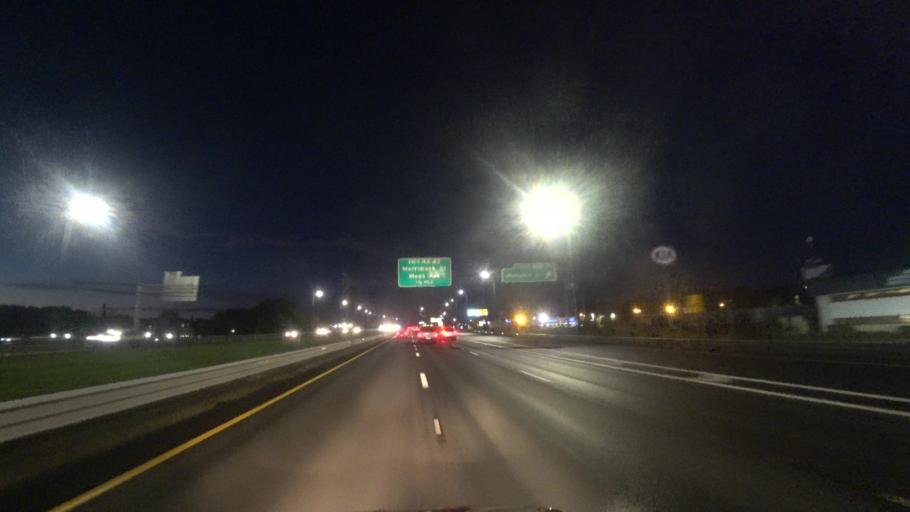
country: US
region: Massachusetts
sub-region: Essex County
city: North Andover
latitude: 42.7171
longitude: -71.1373
